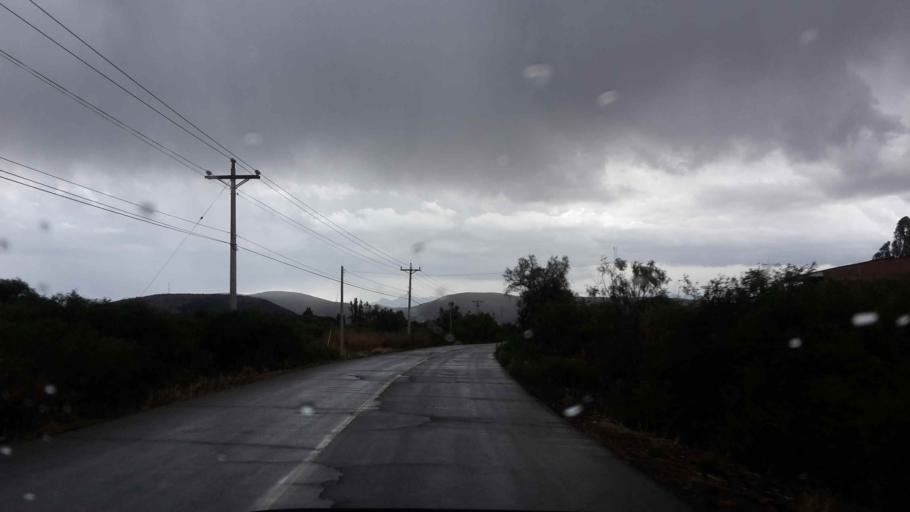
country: BO
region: Cochabamba
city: Tarata
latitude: -17.5670
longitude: -66.0768
